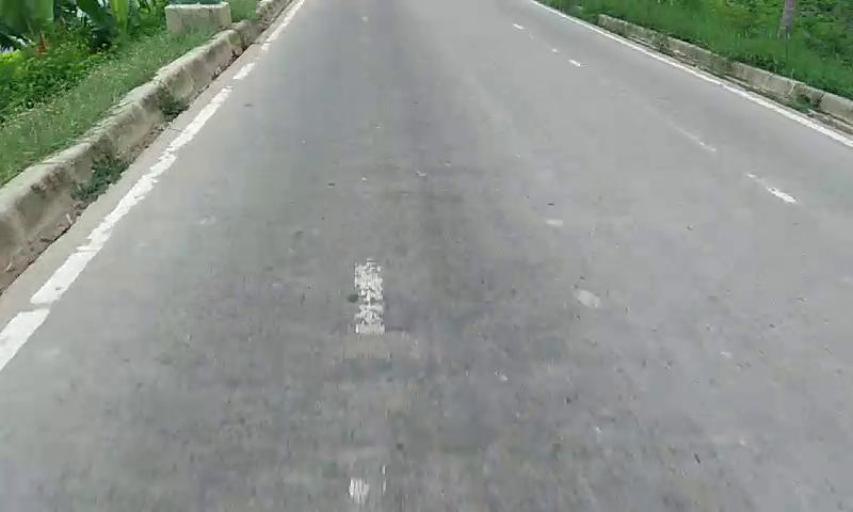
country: ID
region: West Java
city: Bekasi
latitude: -6.1423
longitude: 106.9699
